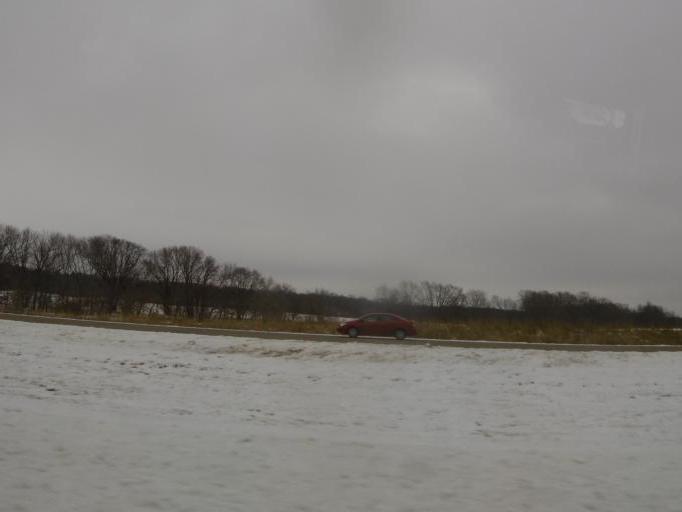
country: US
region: Illinois
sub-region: Hancock County
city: Nauvoo
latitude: 40.5585
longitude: -91.5653
